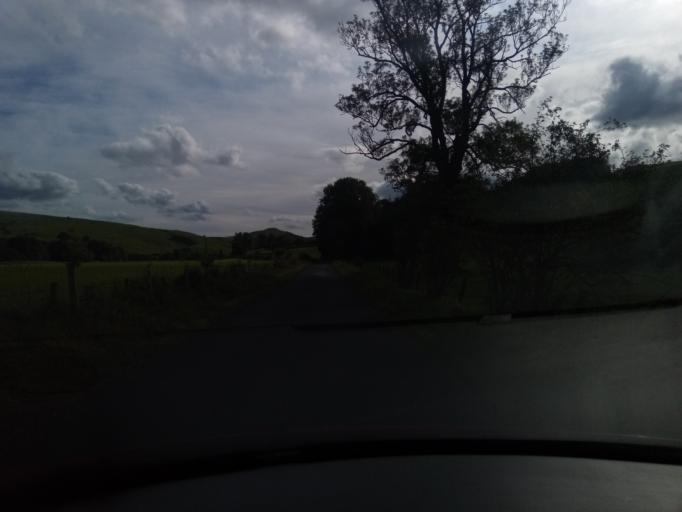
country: GB
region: Scotland
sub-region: The Scottish Borders
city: Kelso
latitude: 55.4902
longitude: -2.3480
